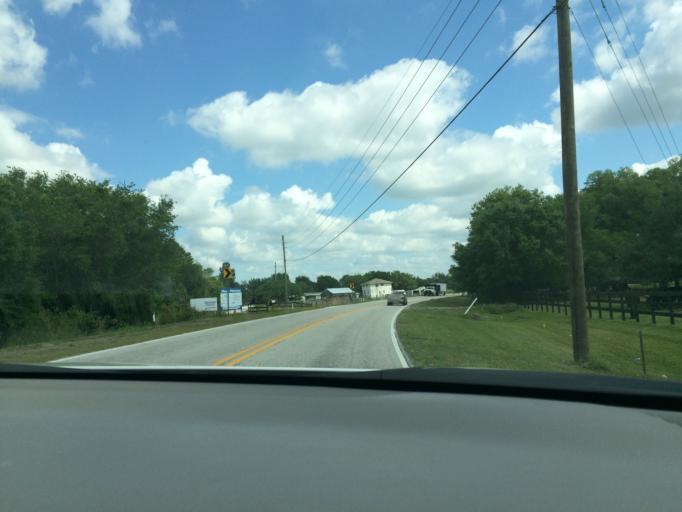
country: US
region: Florida
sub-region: Manatee County
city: Ellenton
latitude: 27.5110
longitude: -82.4335
